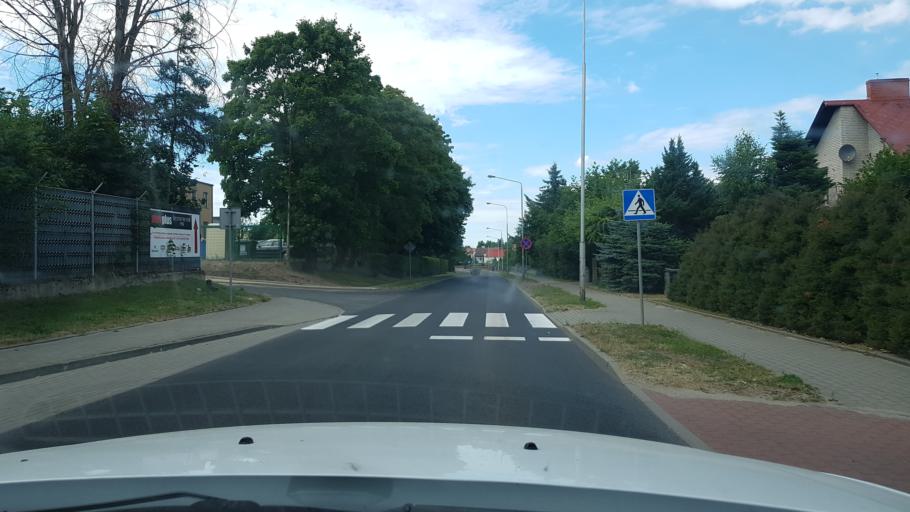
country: PL
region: West Pomeranian Voivodeship
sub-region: Powiat drawski
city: Zlocieniec
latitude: 53.5235
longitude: 16.0160
